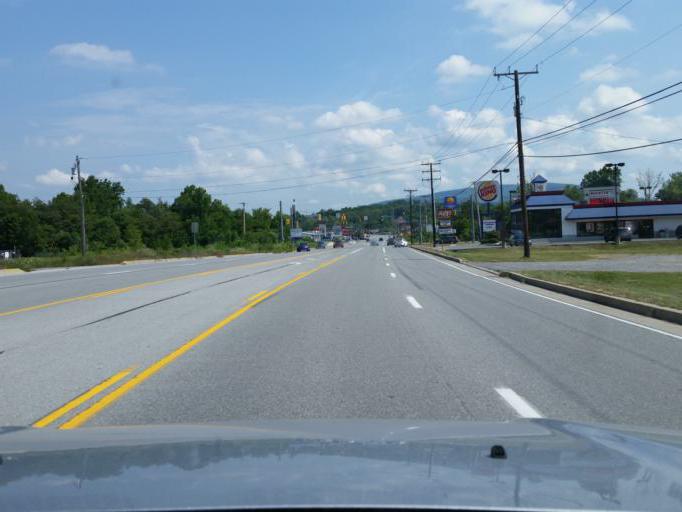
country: US
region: Pennsylvania
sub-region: Blair County
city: Duncansville
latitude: 40.4312
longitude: -78.4171
